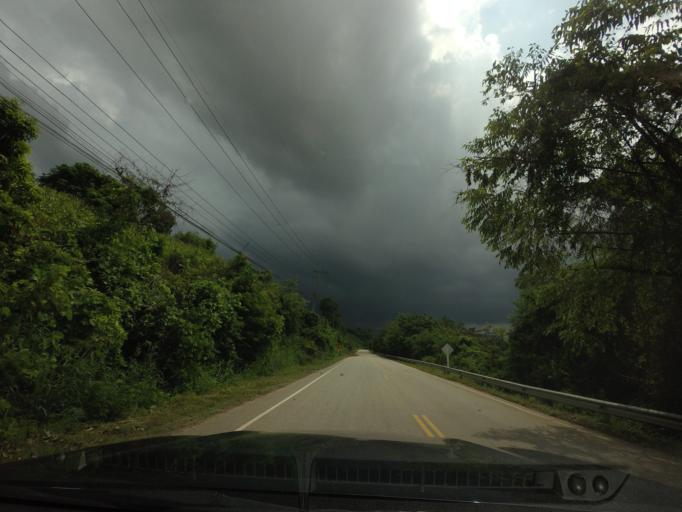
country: LA
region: Vientiane
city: Muang Sanakham
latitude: 17.9753
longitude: 101.7472
